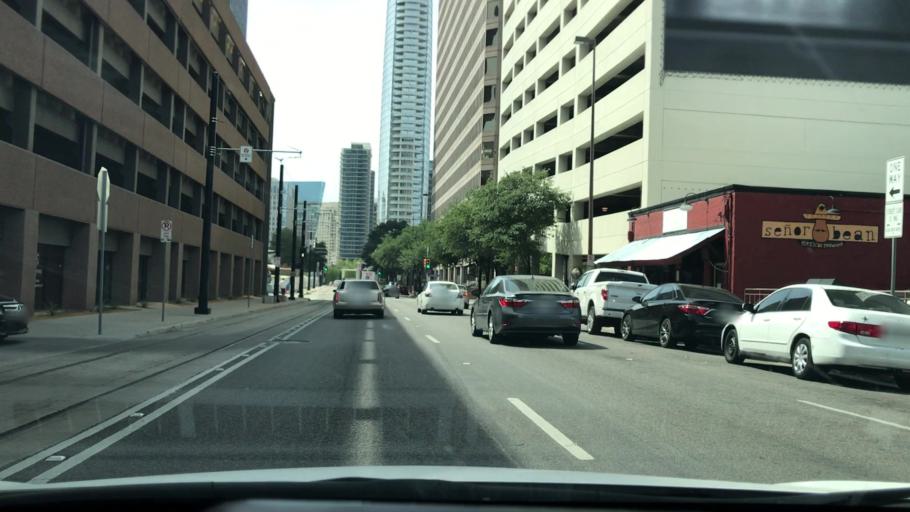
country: US
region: Texas
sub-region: Dallas County
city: Dallas
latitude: 32.7863
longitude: -96.7967
